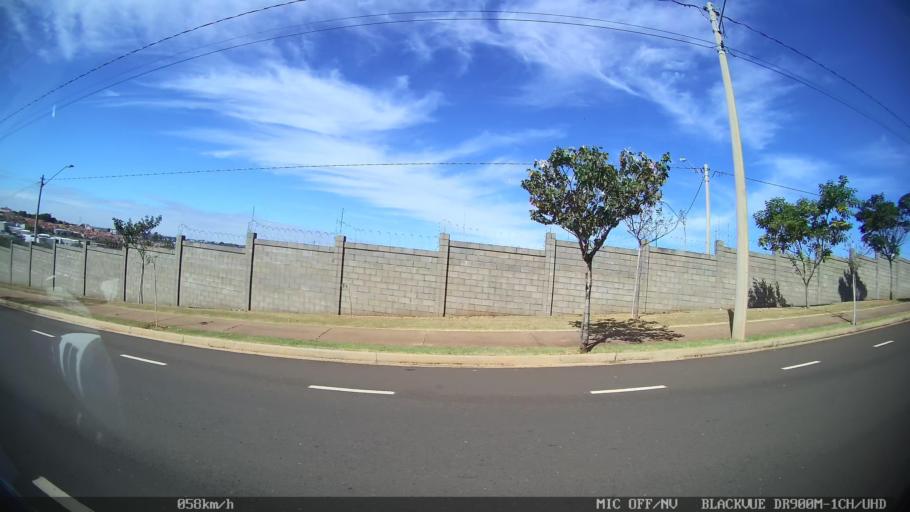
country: BR
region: Sao Paulo
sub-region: Sao Jose Do Rio Preto
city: Sao Jose do Rio Preto
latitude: -20.8501
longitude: -49.3745
